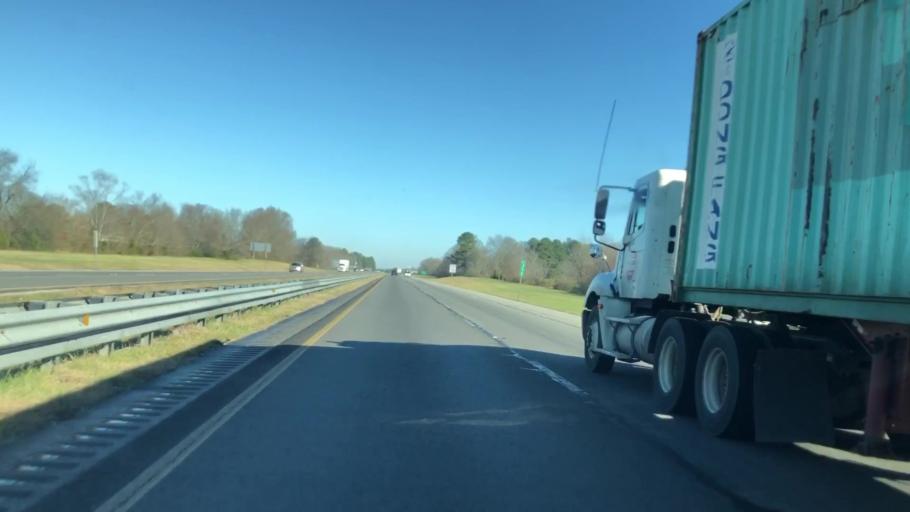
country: US
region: Alabama
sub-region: Limestone County
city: Athens
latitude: 34.8395
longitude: -86.9352
